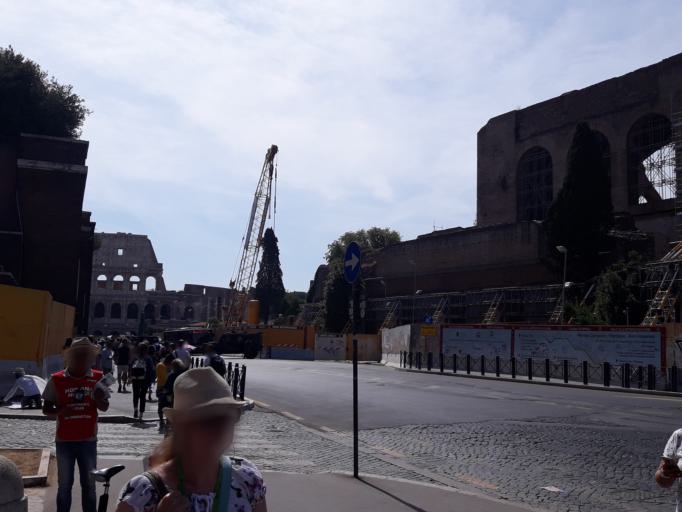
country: IT
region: Latium
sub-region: Citta metropolitana di Roma Capitale
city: Rome
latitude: 41.8927
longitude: 12.4885
